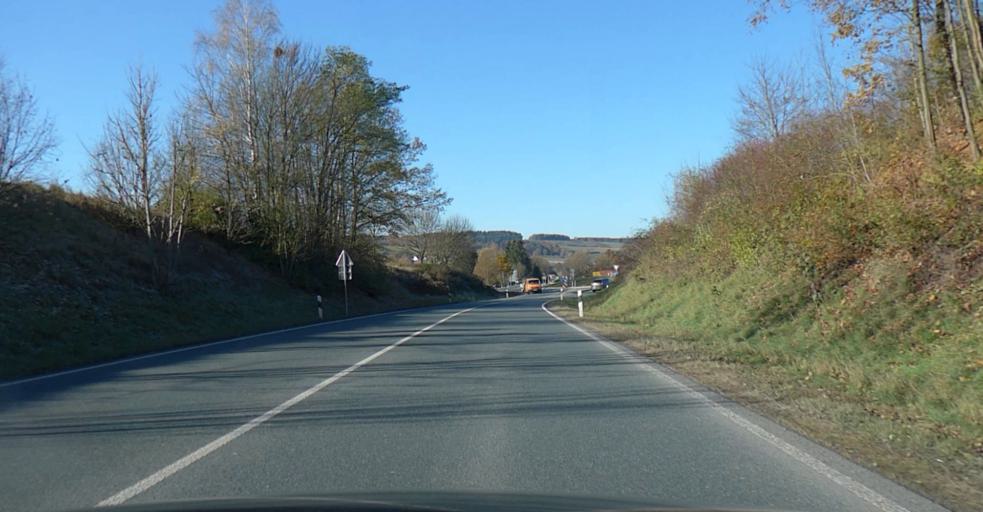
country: DE
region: Bavaria
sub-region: Upper Franconia
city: Untersteinach
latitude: 50.1318
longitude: 11.5397
